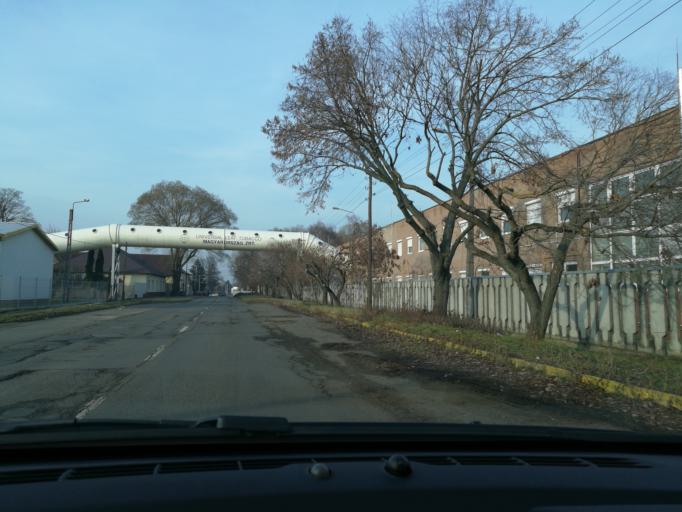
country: HU
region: Szabolcs-Szatmar-Bereg
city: Nyiregyhaza
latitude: 47.9491
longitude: 21.7006
